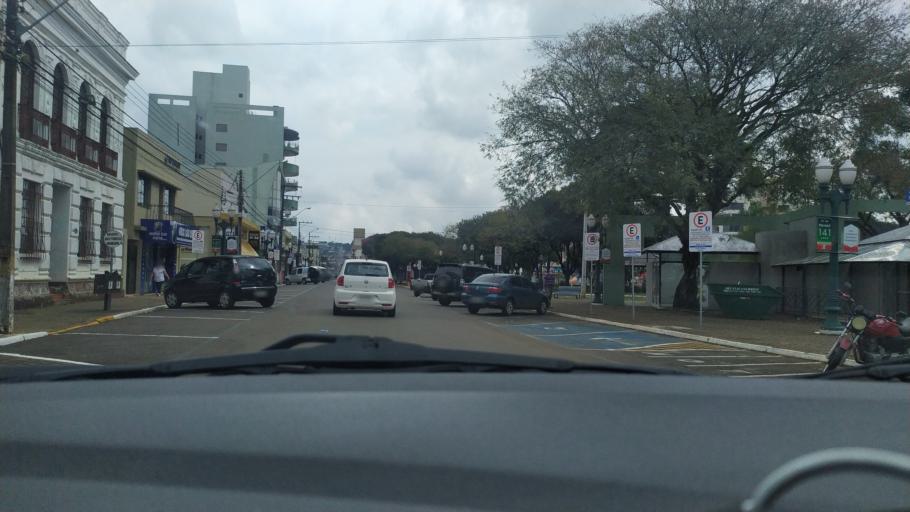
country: BR
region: Parana
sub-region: Palmas
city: Palmas
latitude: -26.4841
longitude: -51.9918
